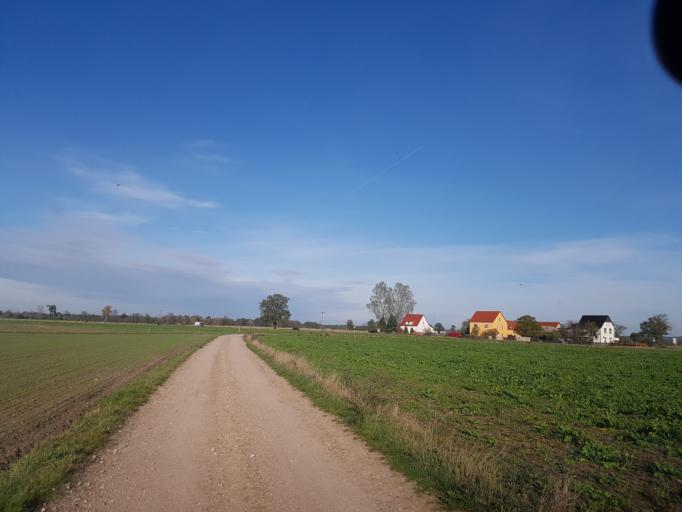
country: DE
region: Saxony
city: Nauwalde
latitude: 51.4628
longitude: 13.4276
